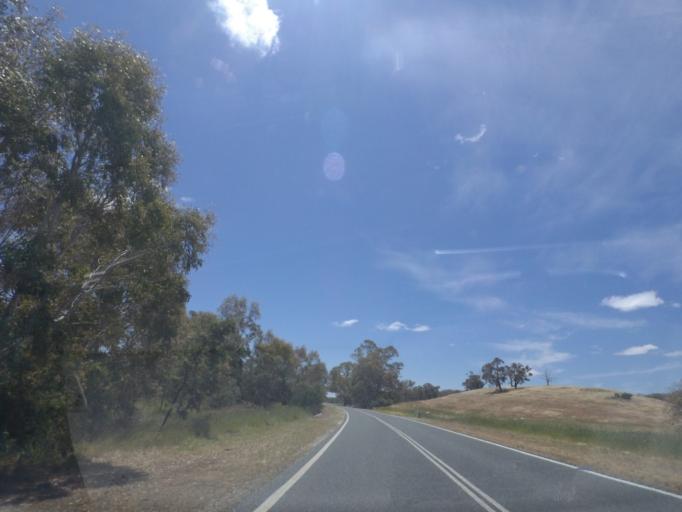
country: AU
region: Victoria
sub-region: Mount Alexander
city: Castlemaine
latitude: -37.1902
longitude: 144.1491
